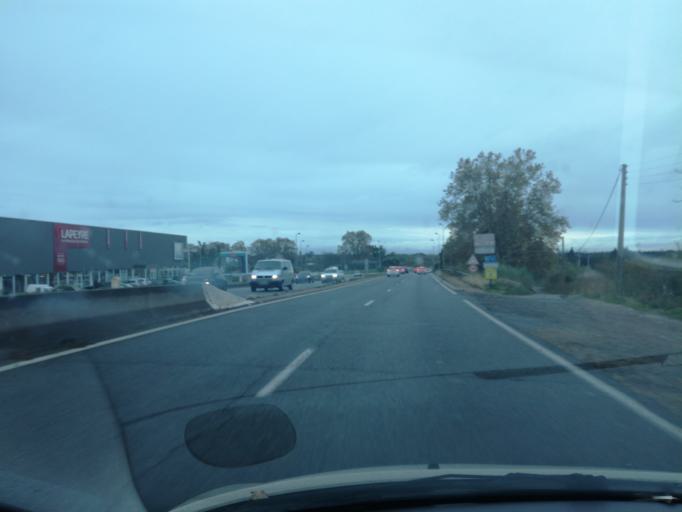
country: FR
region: Provence-Alpes-Cote d'Azur
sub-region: Departement du Var
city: Puget-sur-Argens
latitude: 43.4410
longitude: 6.7058
